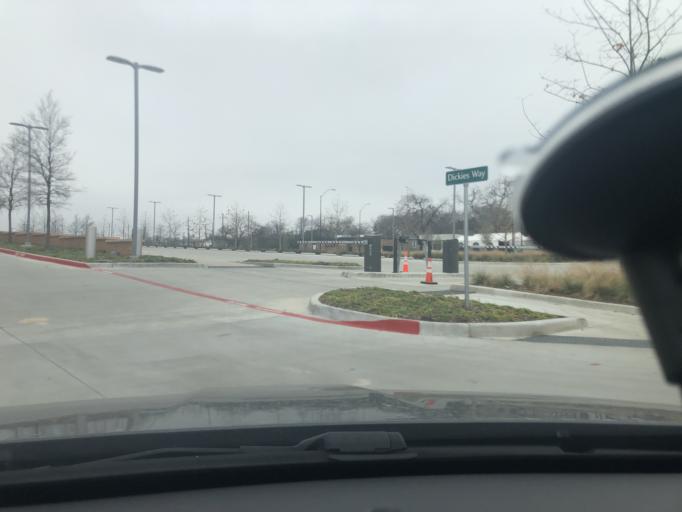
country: US
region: Texas
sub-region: Tarrant County
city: River Oaks
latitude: 32.7422
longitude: -97.3693
